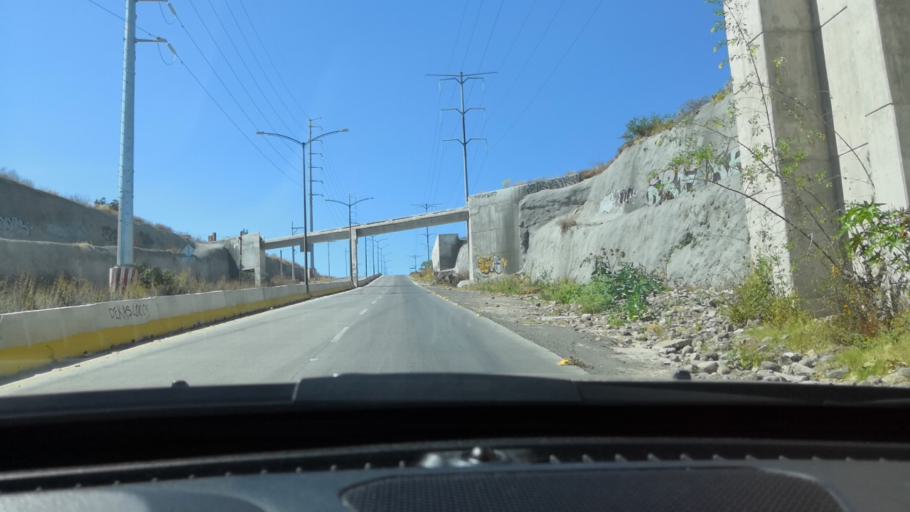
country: MX
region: Guanajuato
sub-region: Leon
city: Centro Familiar la Soledad
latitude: 21.1197
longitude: -101.7442
